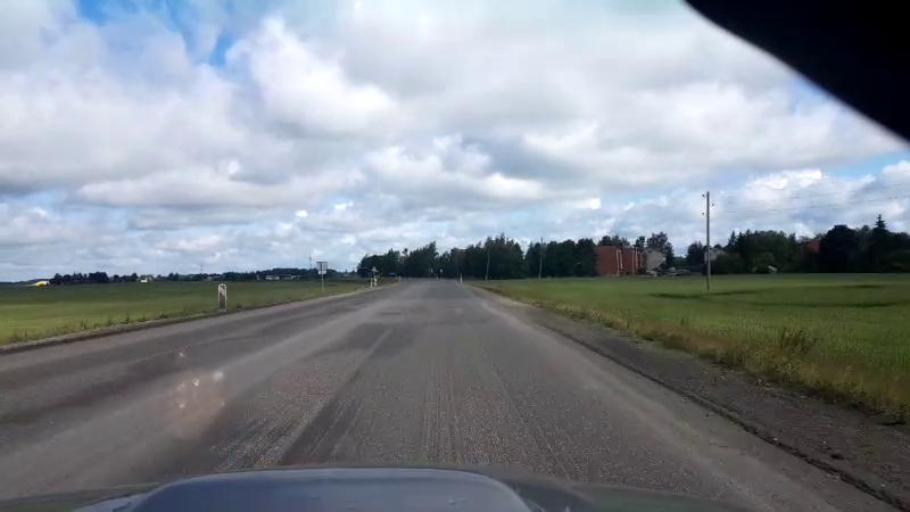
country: LV
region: Bauskas Rajons
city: Bauska
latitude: 56.3095
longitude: 24.3379
